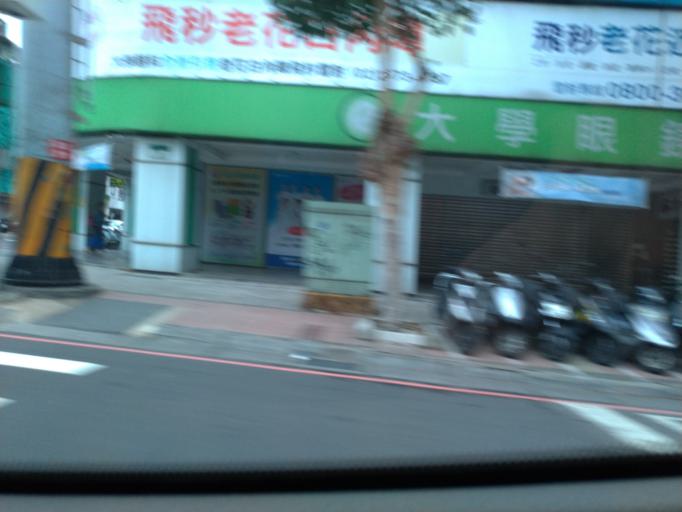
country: TW
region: Taiwan
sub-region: Taoyuan
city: Taoyuan
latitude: 24.9359
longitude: 121.3743
